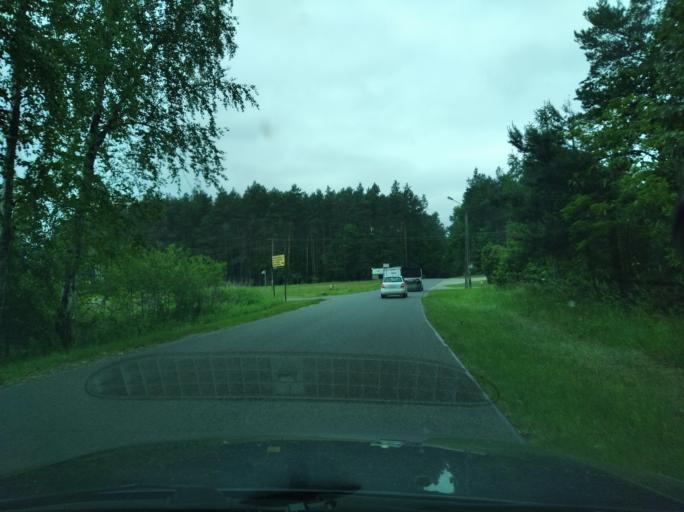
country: PL
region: Subcarpathian Voivodeship
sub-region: Powiat kolbuszowski
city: Niwiska
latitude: 50.1742
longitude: 21.6650
